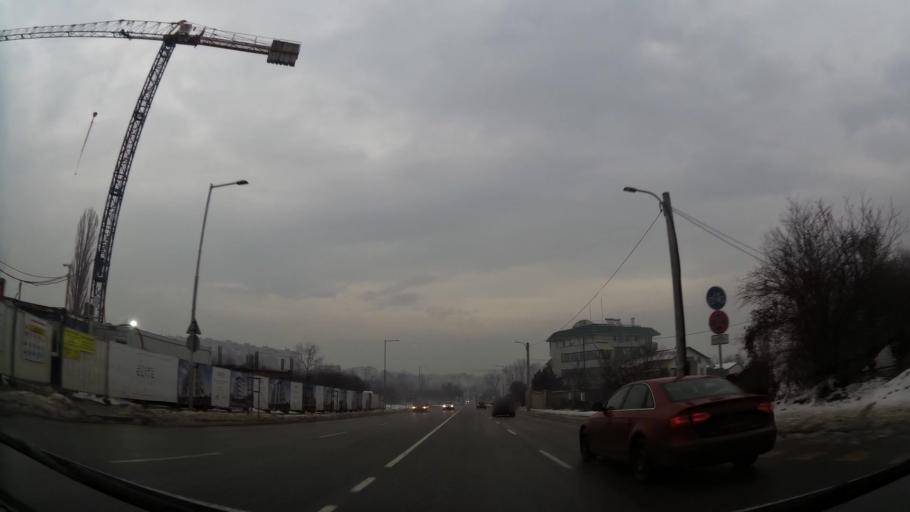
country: BG
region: Sofia-Capital
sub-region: Stolichna Obshtina
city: Sofia
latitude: 42.6807
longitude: 23.2549
